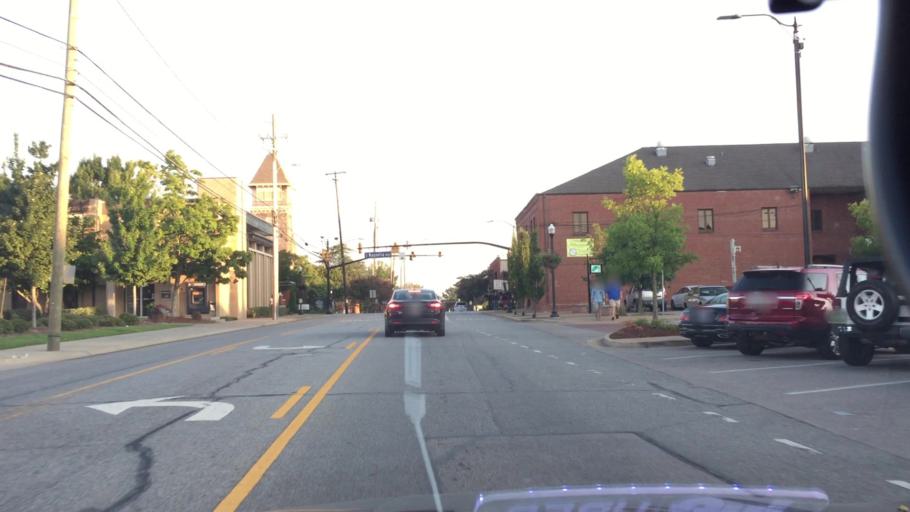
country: US
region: Alabama
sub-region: Lee County
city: Auburn
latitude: 32.6074
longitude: -85.4799
